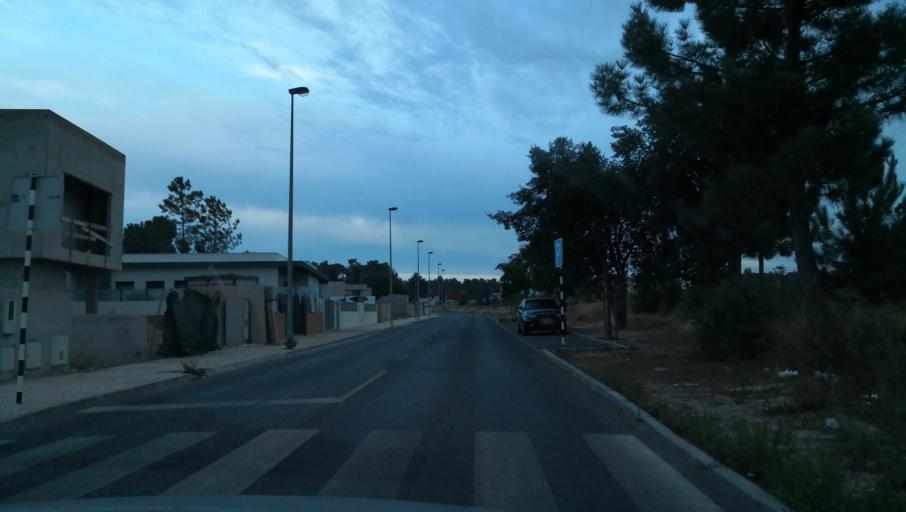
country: PT
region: Setubal
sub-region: Seixal
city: Amora
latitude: 38.5965
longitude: -9.1478
